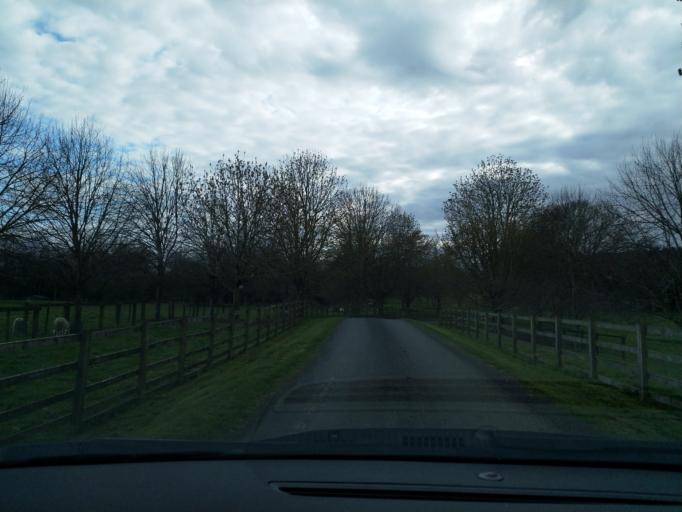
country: GB
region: England
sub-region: Warwickshire
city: Wellesbourne Mountford
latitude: 52.1708
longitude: -1.5535
